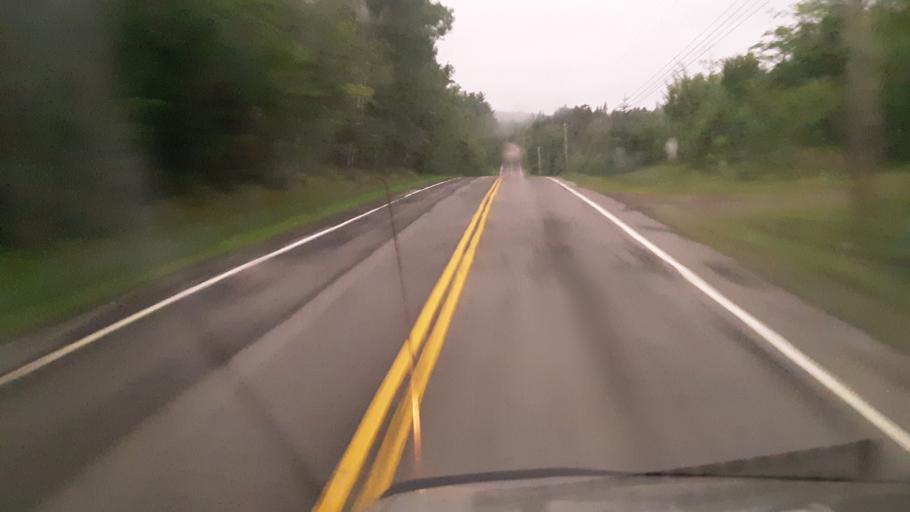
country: US
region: Maine
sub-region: Penobscot County
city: Patten
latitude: 46.1051
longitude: -68.4168
